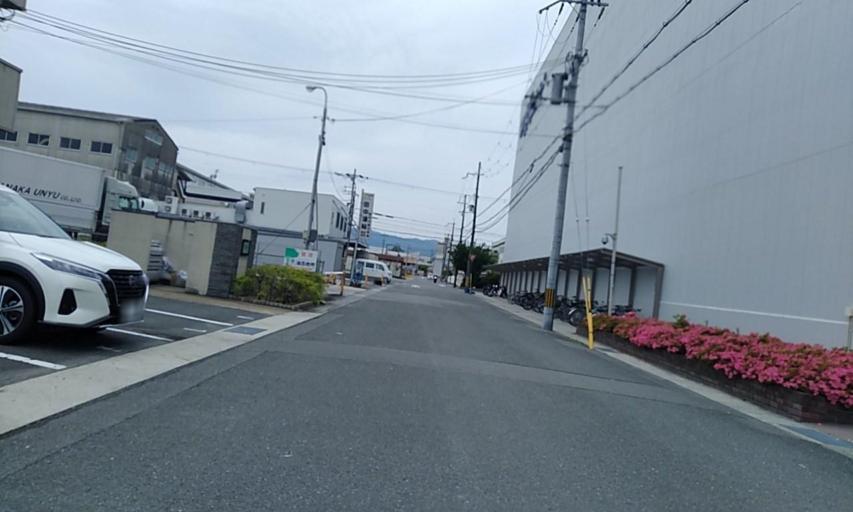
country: JP
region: Kyoto
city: Muko
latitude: 34.9427
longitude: 135.7475
